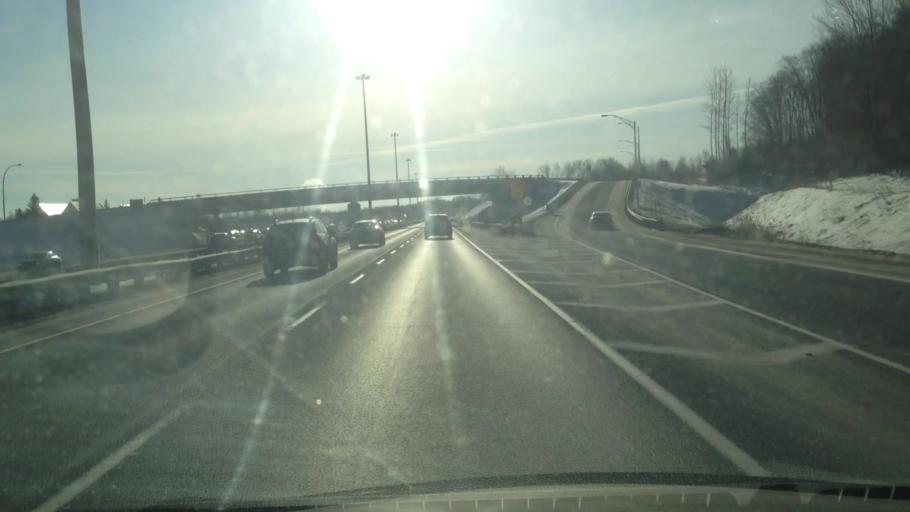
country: CA
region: Quebec
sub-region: Laurentides
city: Prevost
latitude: 45.8442
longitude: -74.0708
